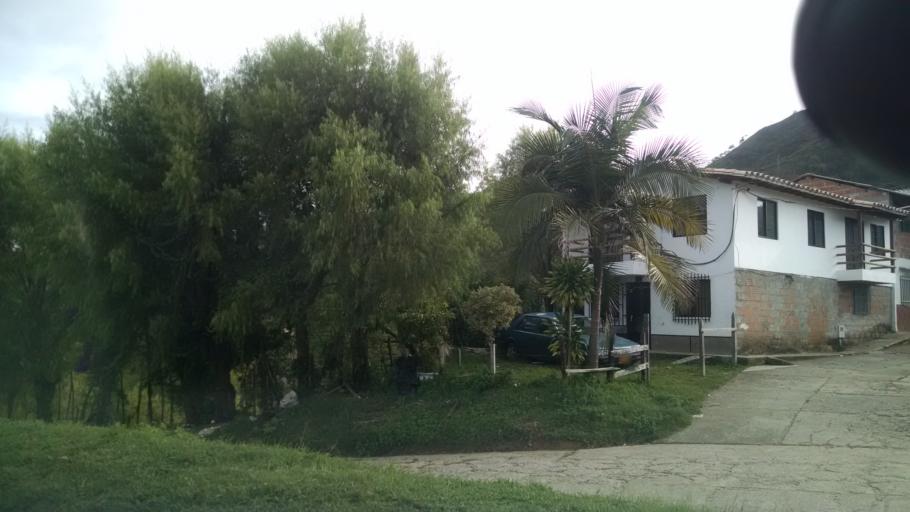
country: CO
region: Antioquia
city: Guatape
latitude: 6.2152
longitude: -75.2385
